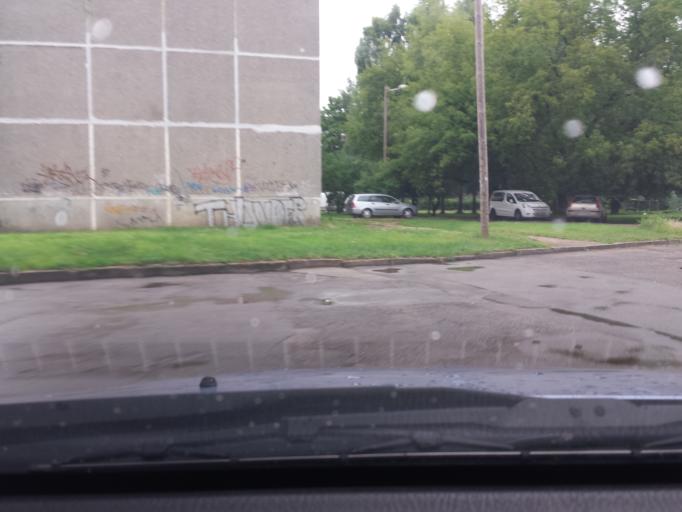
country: LV
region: Kekava
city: Kekava
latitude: 56.9033
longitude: 24.2026
